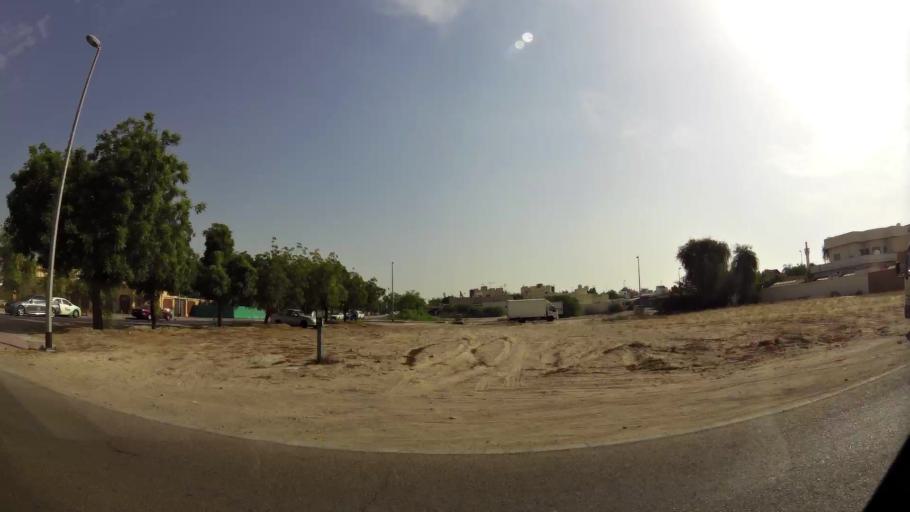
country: AE
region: Ash Shariqah
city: Sharjah
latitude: 25.2250
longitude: 55.3944
